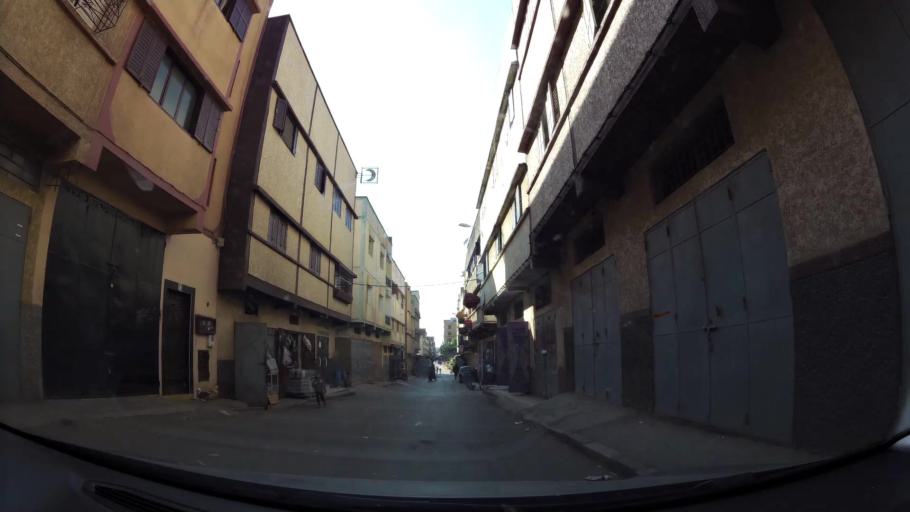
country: MA
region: Rabat-Sale-Zemmour-Zaer
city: Sale
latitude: 34.0530
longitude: -6.7751
